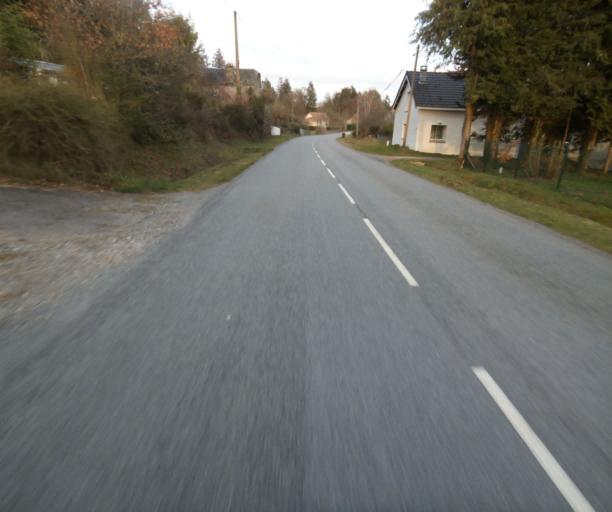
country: FR
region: Limousin
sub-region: Departement de la Correze
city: Correze
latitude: 45.2797
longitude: 1.9467
